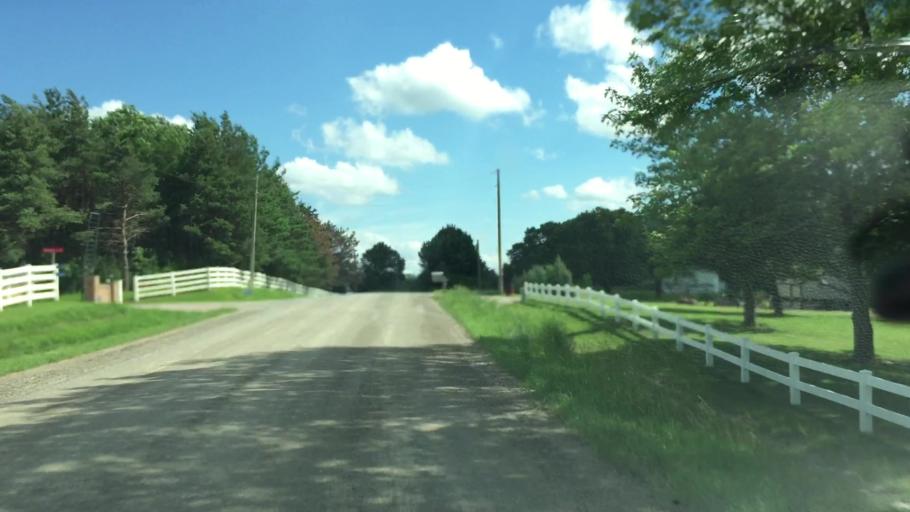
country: US
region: Iowa
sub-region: Linn County
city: Ely
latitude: 41.8379
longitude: -91.6106
